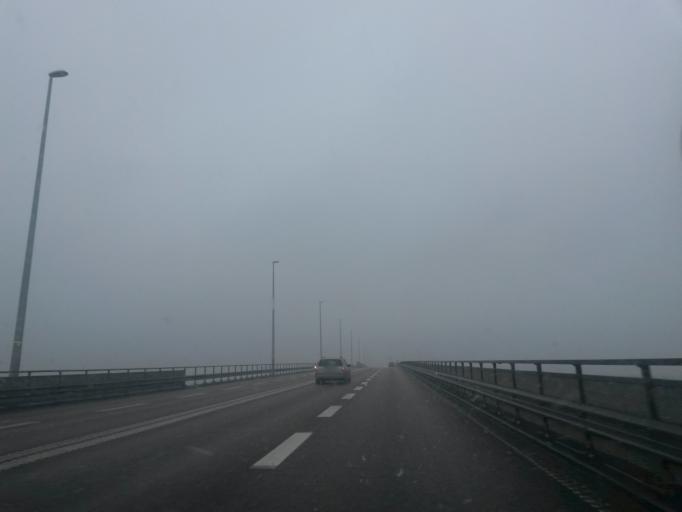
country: SE
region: Vaestra Goetaland
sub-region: Trollhattan
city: Trollhattan
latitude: 58.3076
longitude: 12.3203
